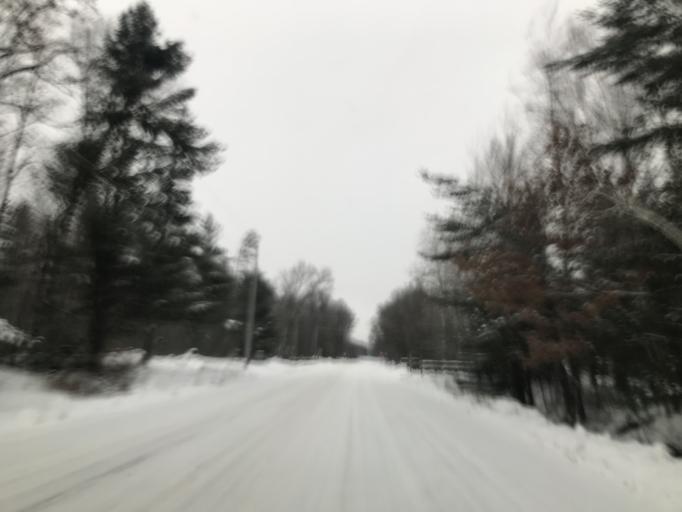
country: US
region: Wisconsin
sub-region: Marinette County
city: Peshtigo
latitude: 45.0415
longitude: -87.7192
